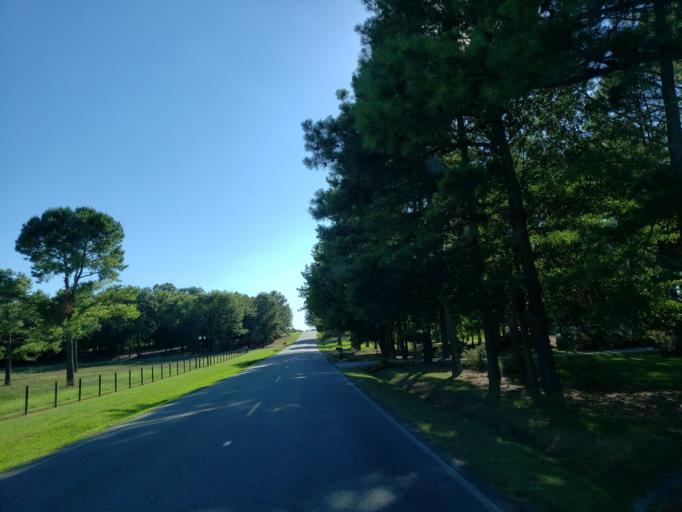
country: US
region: Georgia
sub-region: Bartow County
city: Euharlee
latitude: 34.1051
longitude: -84.9673
